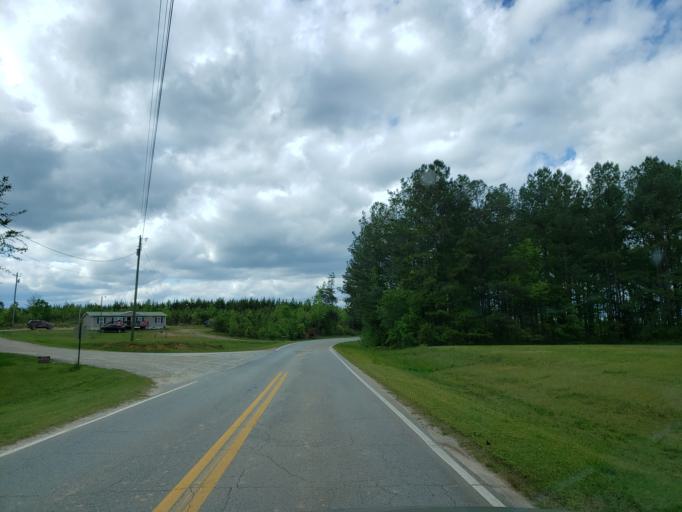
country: US
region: Georgia
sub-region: Haralson County
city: Tallapoosa
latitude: 33.7094
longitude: -85.3296
